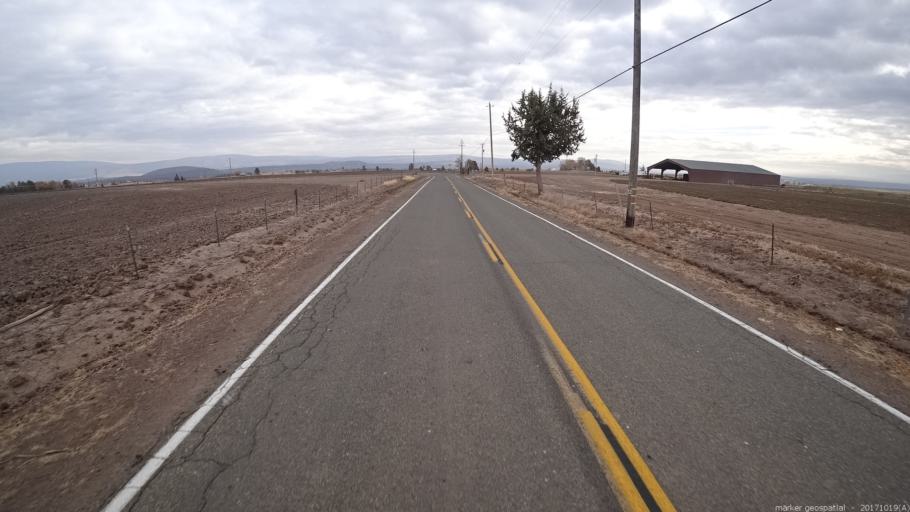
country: US
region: California
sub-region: Shasta County
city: Burney
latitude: 41.0333
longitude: -121.3668
